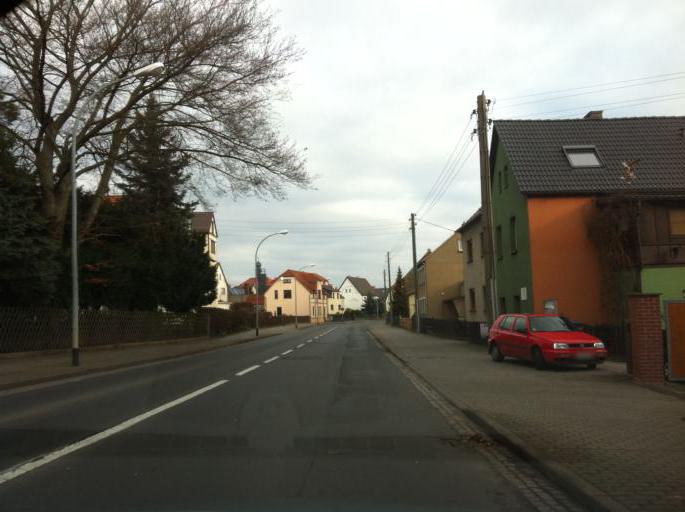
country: DE
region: Saxony
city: Trebsen
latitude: 51.2856
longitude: 12.7535
